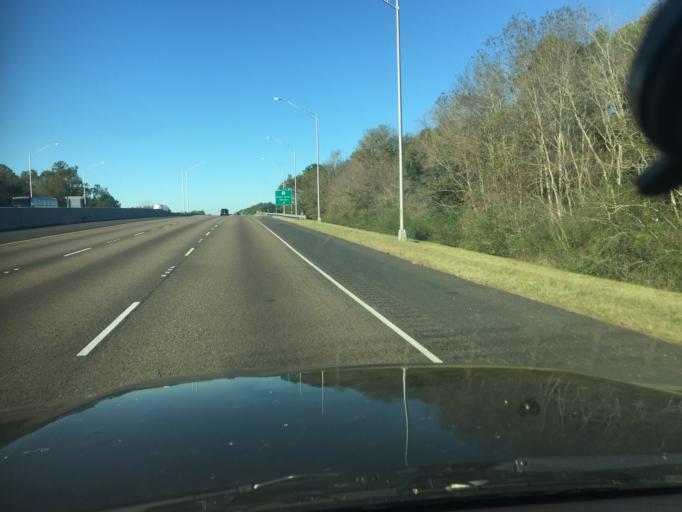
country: US
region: Louisiana
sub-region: Saint Tammany Parish
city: Slidell
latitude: 30.3104
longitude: -89.7677
